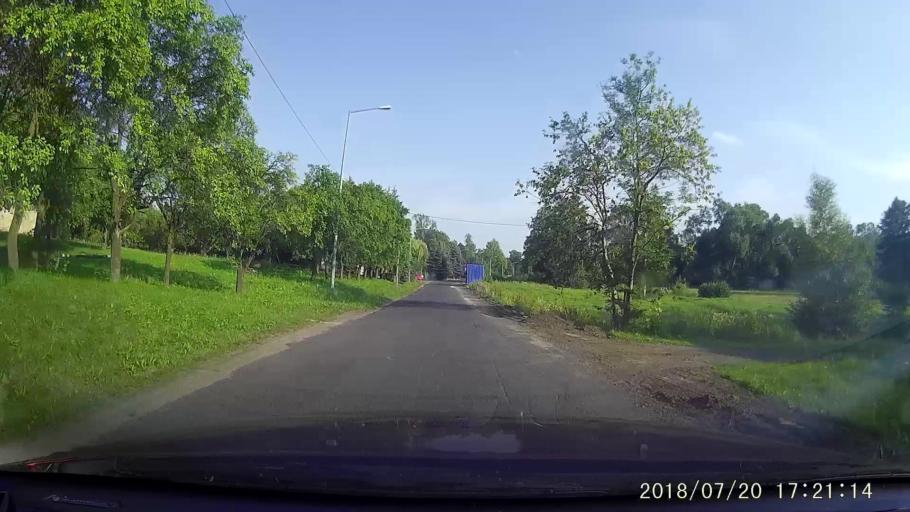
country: PL
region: Lower Silesian Voivodeship
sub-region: Powiat lubanski
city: Lesna
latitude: 50.9845
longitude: 15.2869
